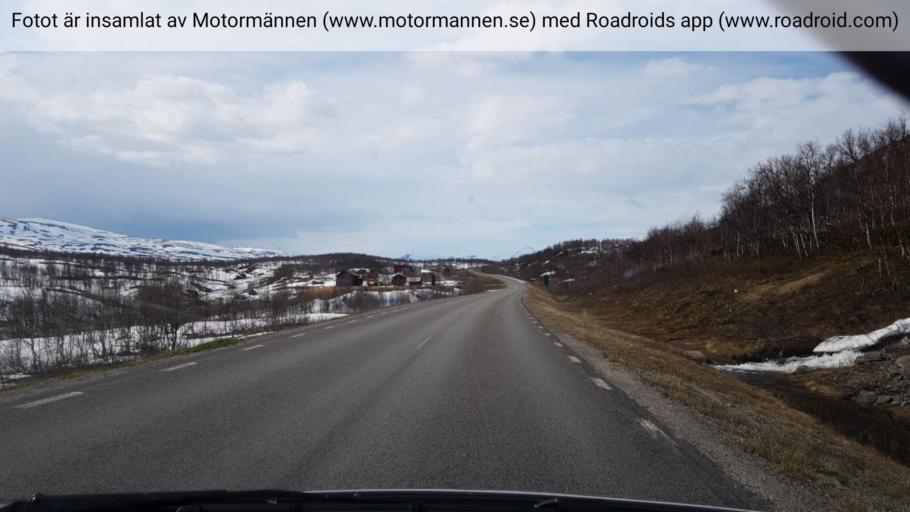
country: NO
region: Nordland
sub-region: Saltdal
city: Rognan
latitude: 66.6761
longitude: 16.1161
